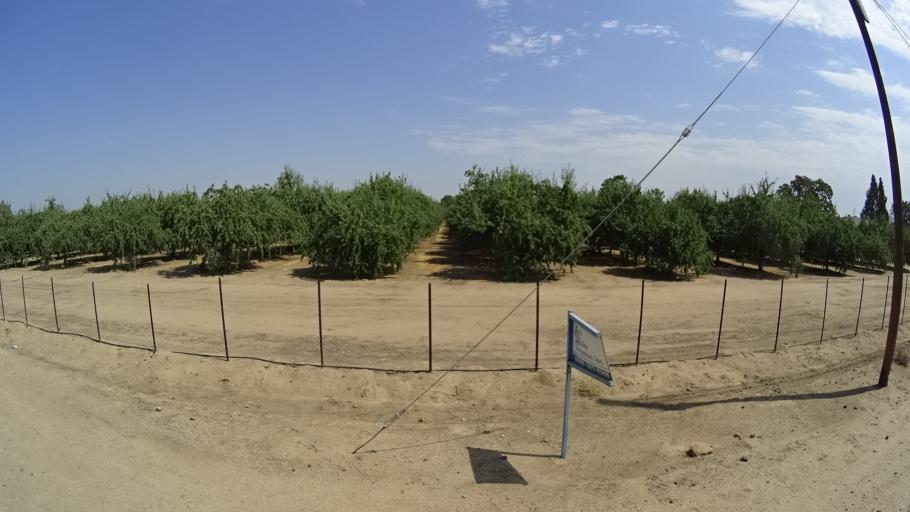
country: US
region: California
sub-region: Fresno County
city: West Park
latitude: 36.7284
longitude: -119.8493
